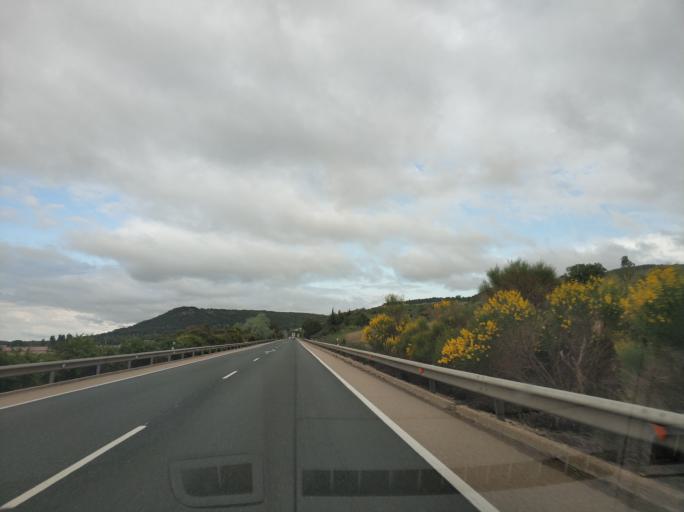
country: ES
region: Castille and Leon
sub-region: Provincia de Valladolid
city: Quintanilla de Onesimo
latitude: 41.6205
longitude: -4.3735
